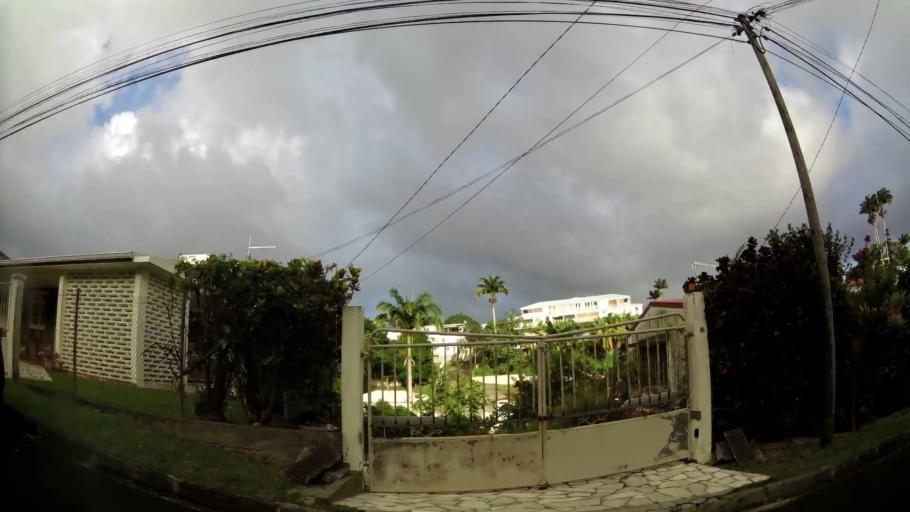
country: MQ
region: Martinique
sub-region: Martinique
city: Fort-de-France
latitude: 14.6260
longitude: -61.0804
